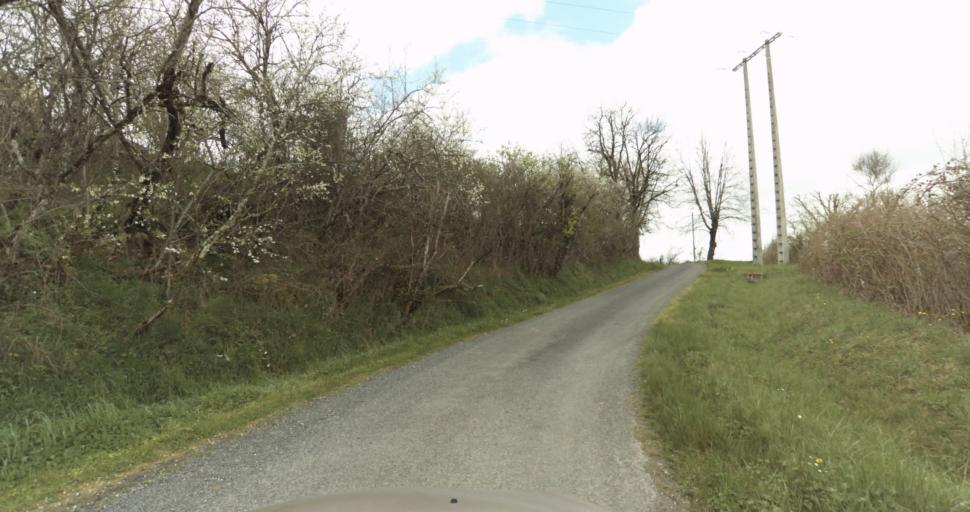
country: FR
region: Midi-Pyrenees
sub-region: Departement du Tarn
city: Puygouzon
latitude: 43.8730
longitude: 2.1703
